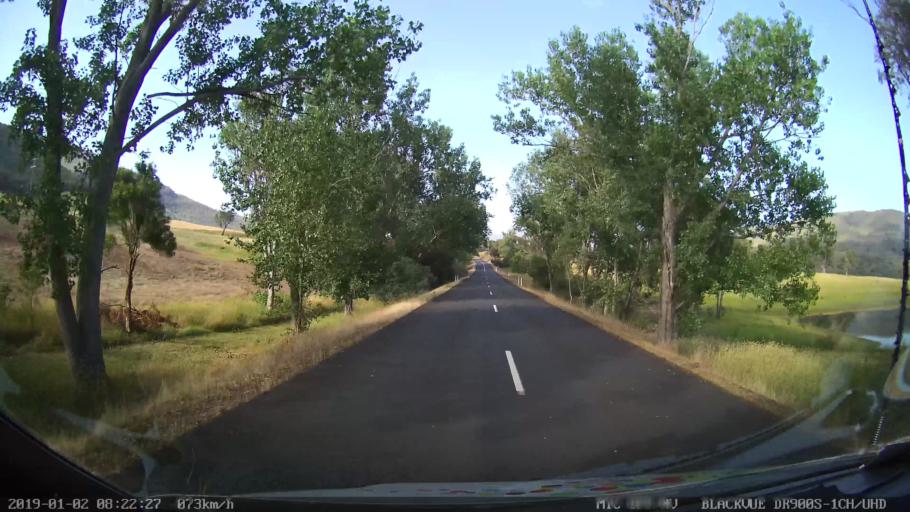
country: AU
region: New South Wales
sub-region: Tumut Shire
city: Tumut
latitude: -35.5710
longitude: 148.3150
